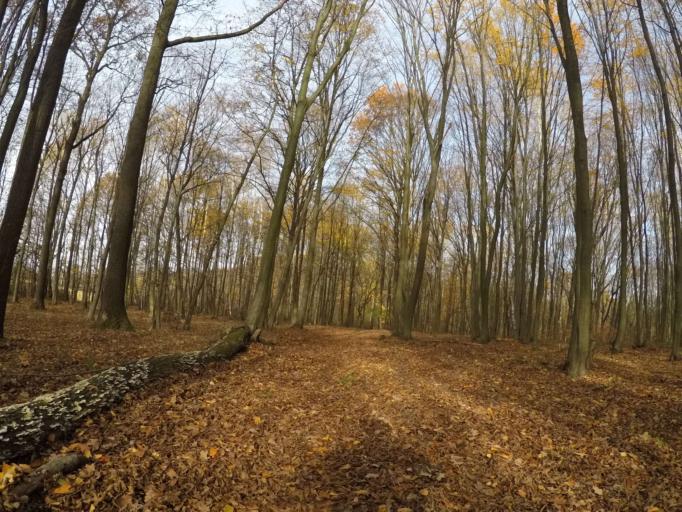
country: SK
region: Presovsky
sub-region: Okres Presov
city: Presov
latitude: 48.9257
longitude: 21.2193
